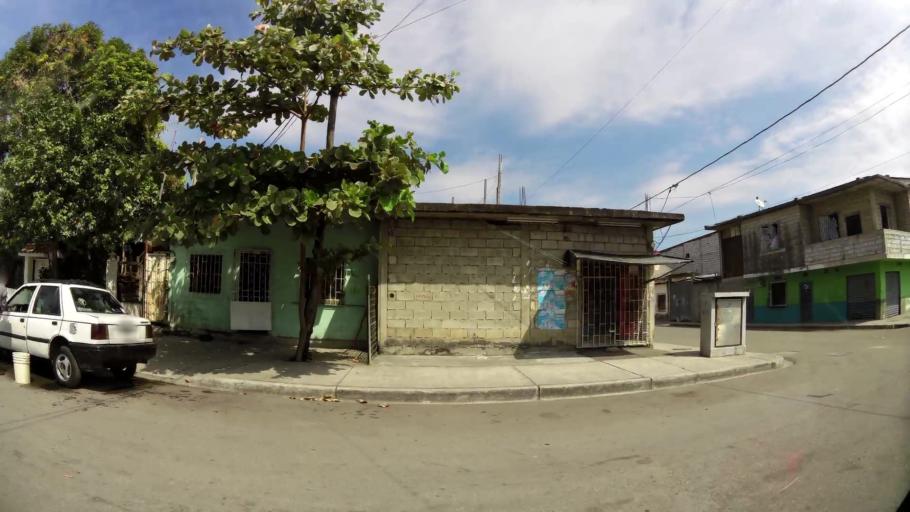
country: EC
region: Guayas
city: Guayaquil
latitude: -2.2643
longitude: -79.8870
